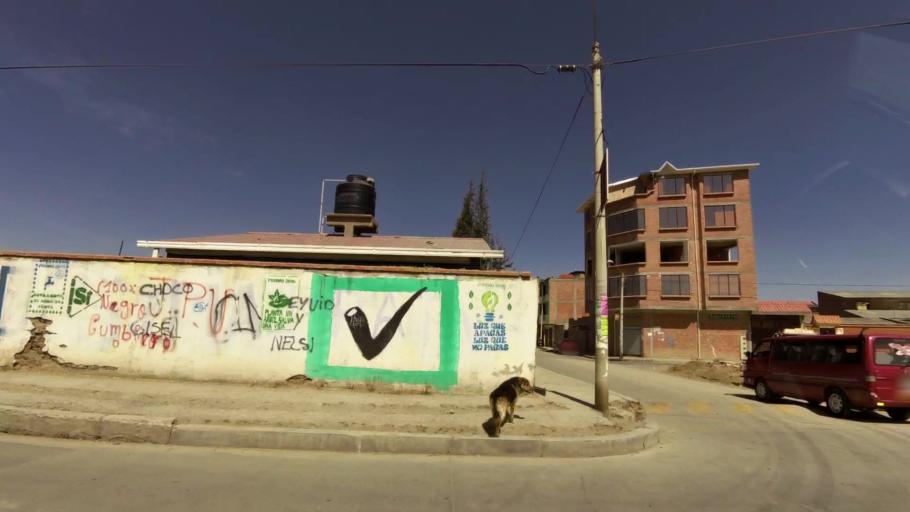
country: BO
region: La Paz
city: La Paz
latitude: -16.5330
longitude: -68.1565
